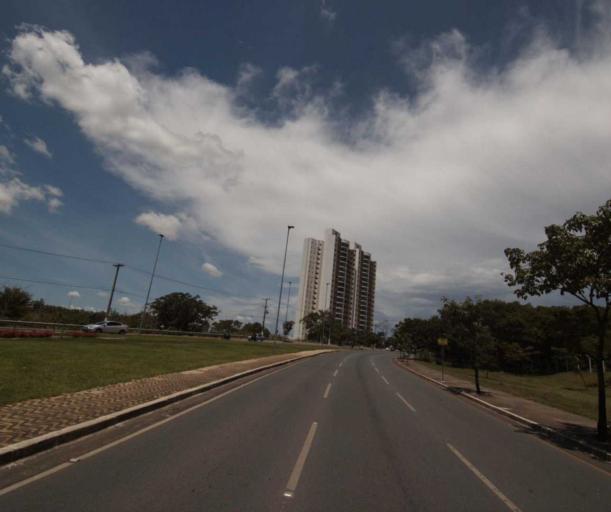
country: BR
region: Mato Grosso
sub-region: Cuiaba
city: Cuiaba
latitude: -15.5757
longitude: -56.1065
